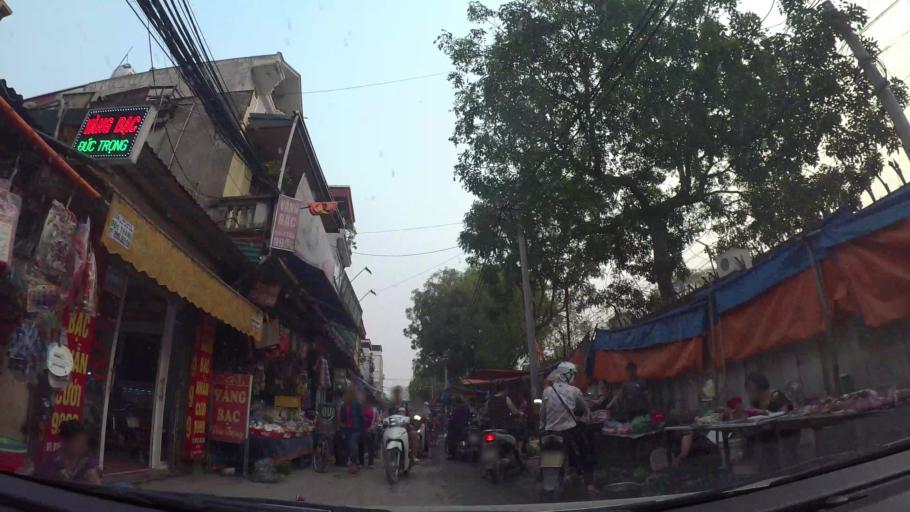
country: VN
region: Ha Noi
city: Ha Dong
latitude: 20.9938
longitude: 105.7298
